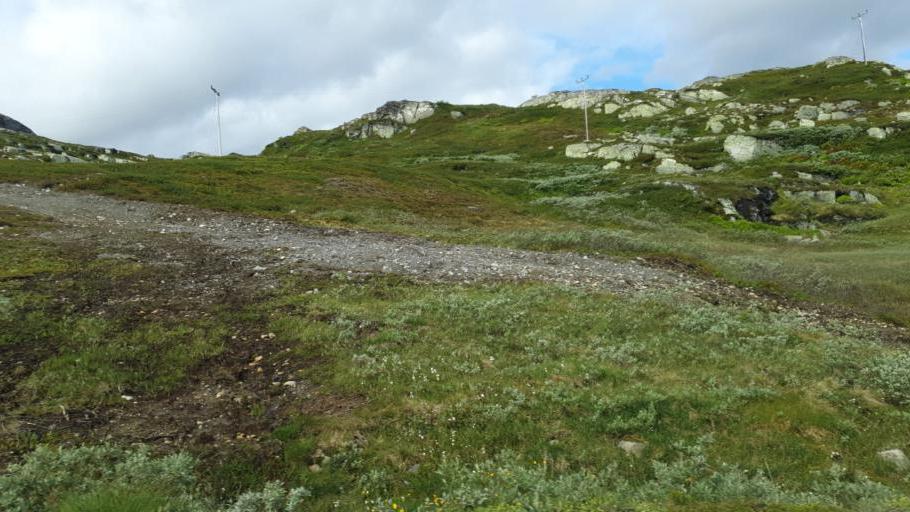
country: NO
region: Oppland
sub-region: Vestre Slidre
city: Slidre
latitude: 61.3125
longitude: 8.8080
